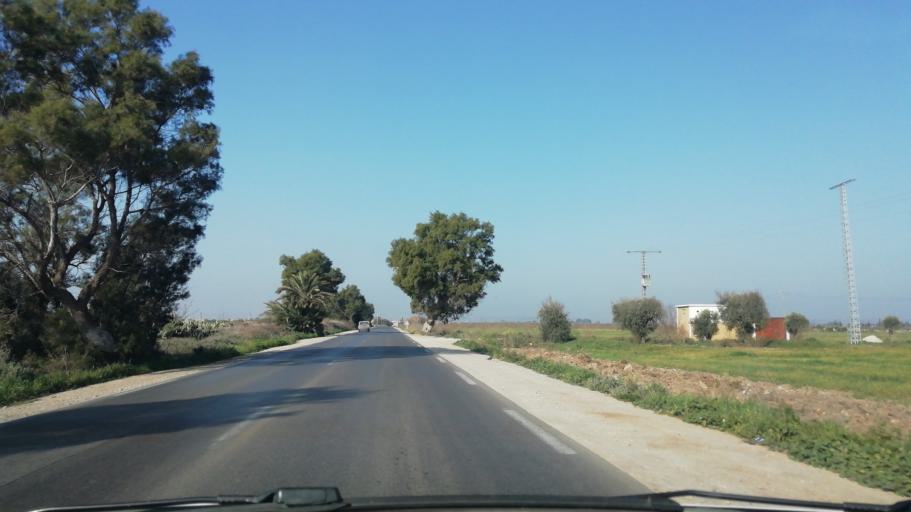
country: DZ
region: Mostaganem
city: Mostaganem
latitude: 35.7592
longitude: 0.0715
